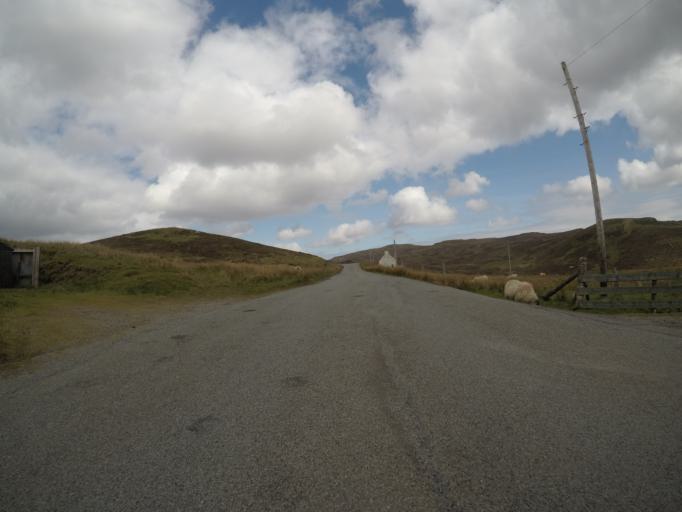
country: GB
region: Scotland
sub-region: Highland
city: Isle of Skye
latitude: 57.3745
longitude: -6.3755
